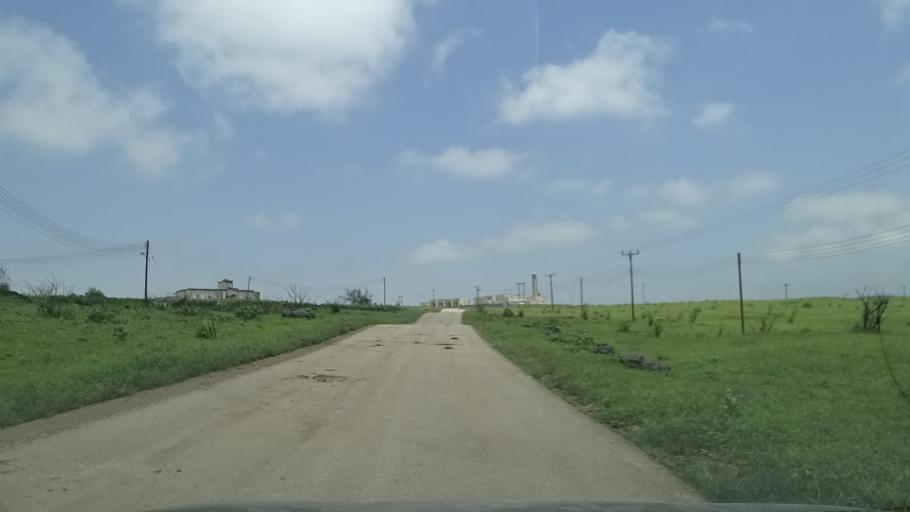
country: OM
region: Zufar
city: Salalah
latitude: 17.2297
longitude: 54.2112
